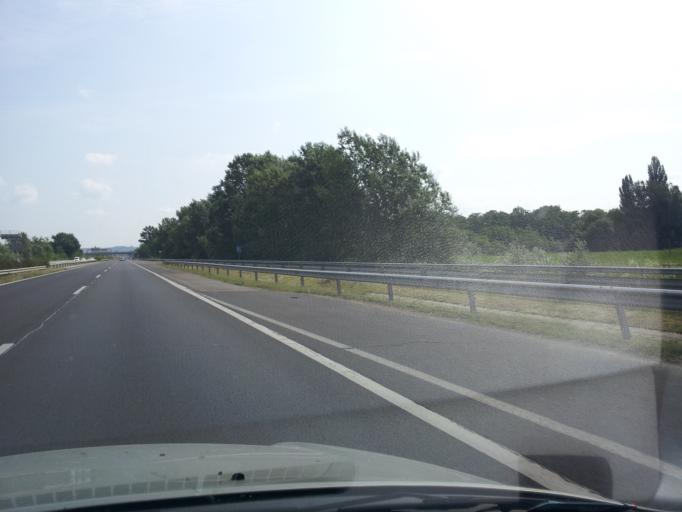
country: HU
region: Budapest
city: Budapest XV. keruelet
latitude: 47.5757
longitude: 19.1612
